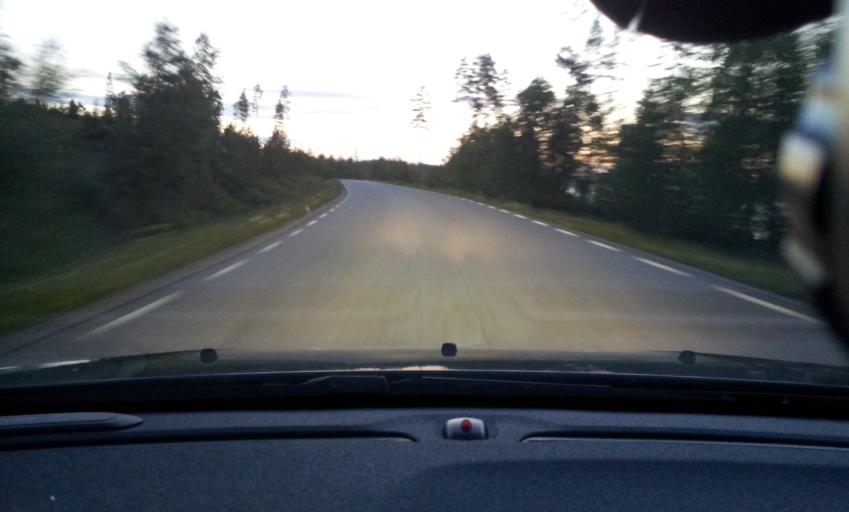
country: SE
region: Jaemtland
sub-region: Braecke Kommun
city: Braecke
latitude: 62.7378
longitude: 15.3919
